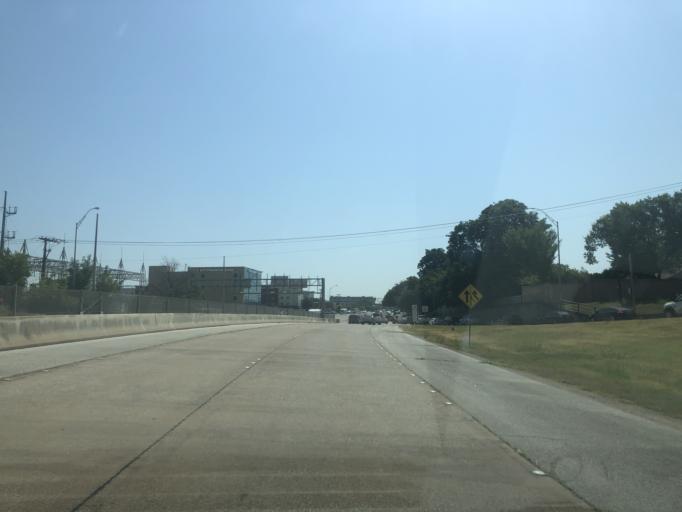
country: US
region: Texas
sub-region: Tarrant County
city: Fort Worth
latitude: 32.7339
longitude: -97.3552
